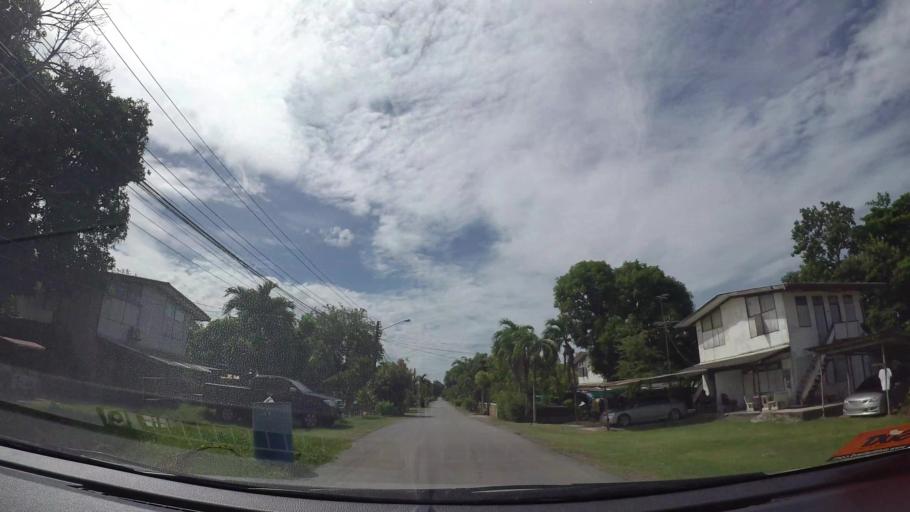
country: TH
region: Chon Buri
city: Sattahip
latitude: 12.6652
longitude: 100.9116
